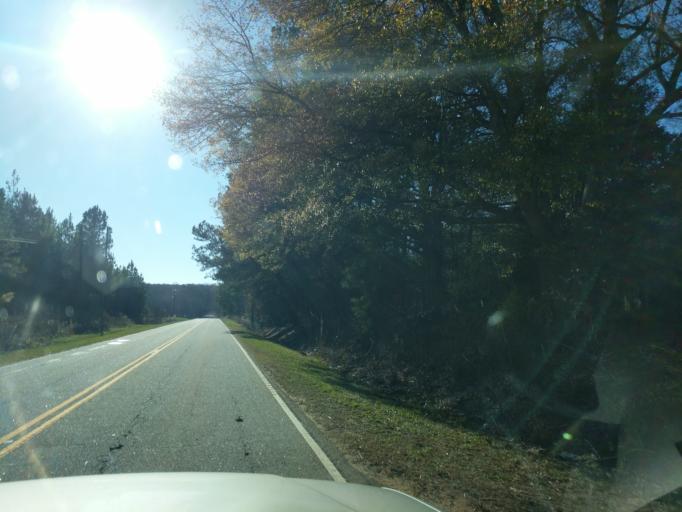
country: US
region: South Carolina
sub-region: Spartanburg County
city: Landrum
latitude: 35.1317
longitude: -82.1182
